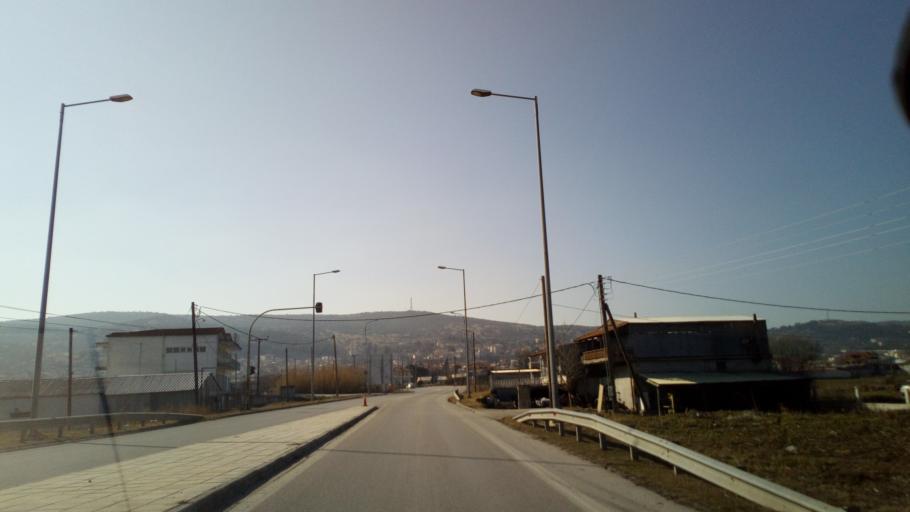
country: GR
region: Central Macedonia
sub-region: Nomos Thessalonikis
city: Lagyna
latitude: 40.7278
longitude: 23.0132
